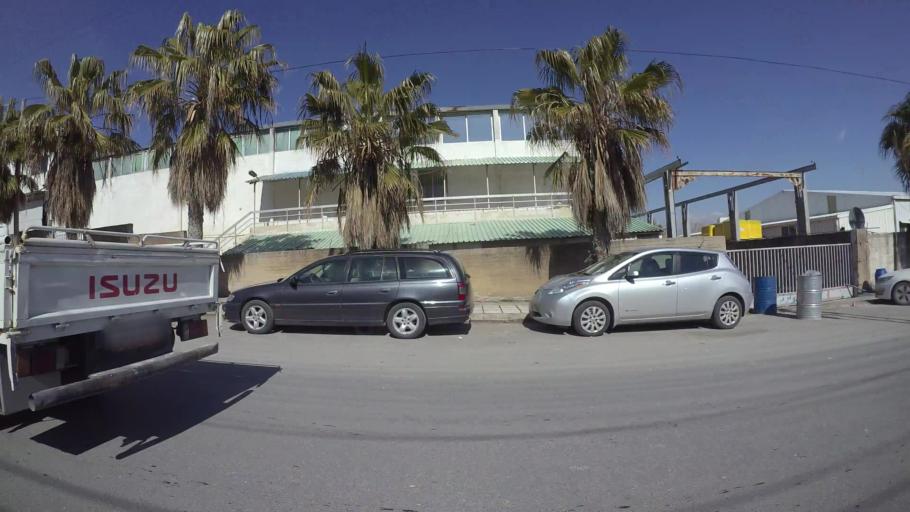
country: JO
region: Amman
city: Al Bunayyat ash Shamaliyah
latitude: 31.9108
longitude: 35.9022
